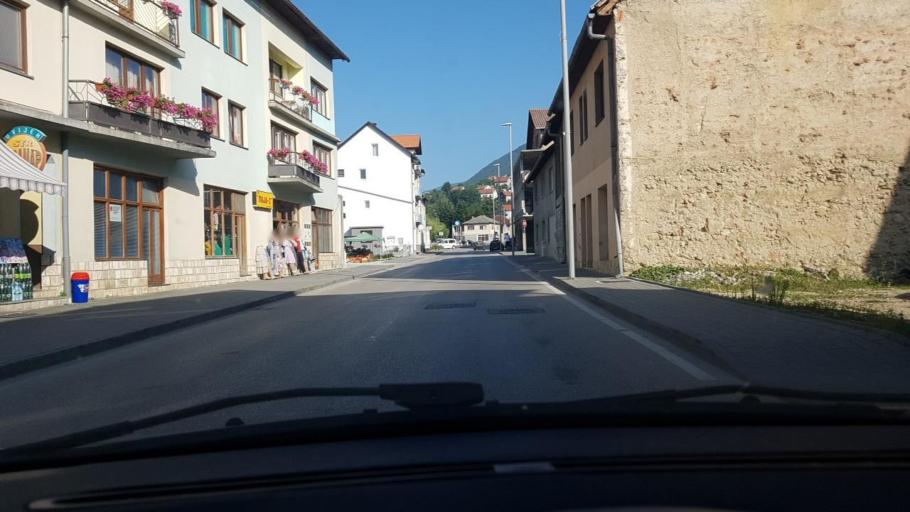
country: BA
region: Federation of Bosnia and Herzegovina
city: Prozor
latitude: 43.8211
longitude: 17.6105
